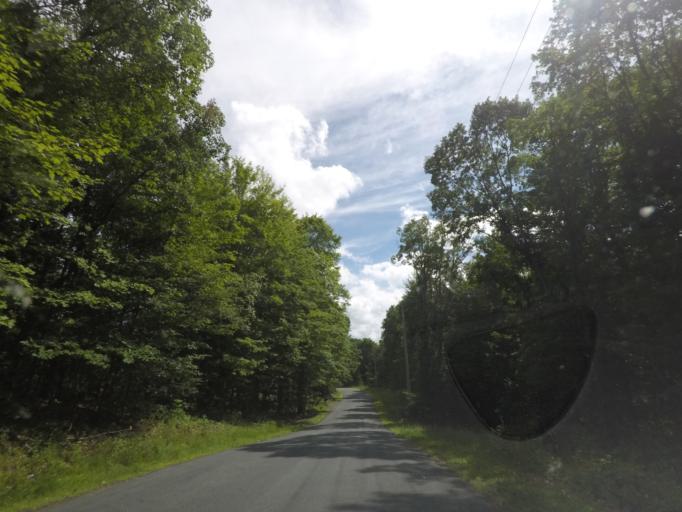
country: US
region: New York
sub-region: Rensselaer County
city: Averill Park
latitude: 42.6624
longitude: -73.5499
